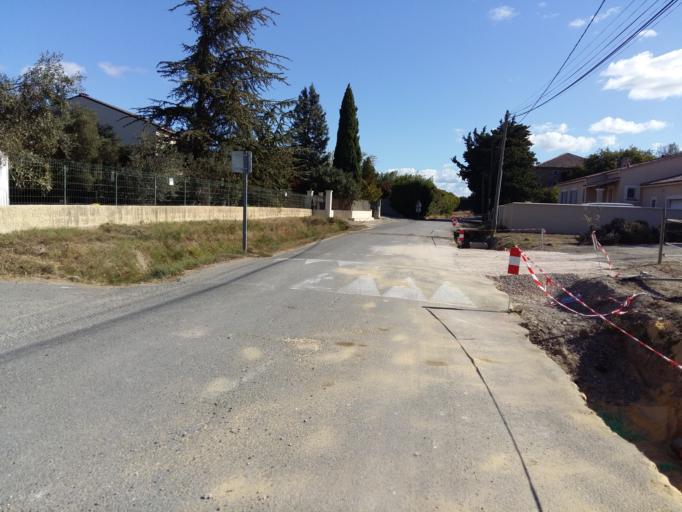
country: FR
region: Provence-Alpes-Cote d'Azur
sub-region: Departement du Vaucluse
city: Piolenc
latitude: 44.1803
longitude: 4.7726
